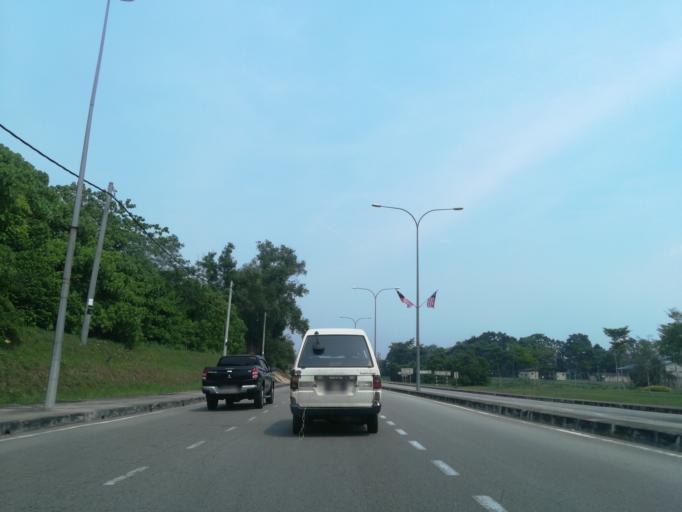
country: MY
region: Kedah
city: Kulim
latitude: 5.3869
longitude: 100.5696
